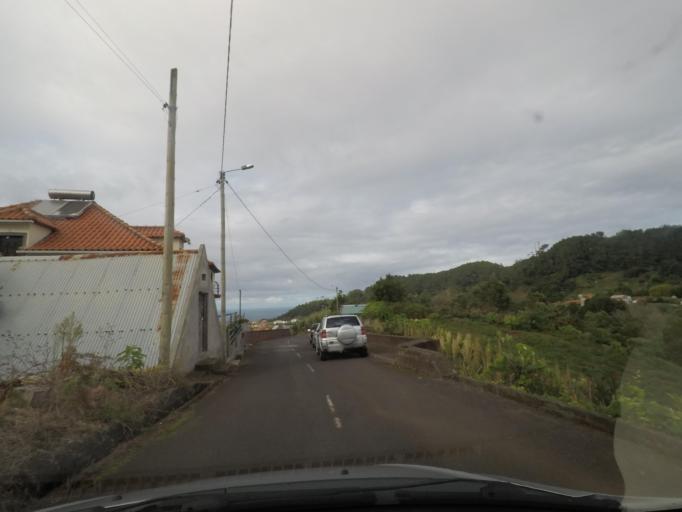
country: PT
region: Madeira
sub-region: Santana
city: Santana
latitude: 32.7991
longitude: -16.8751
